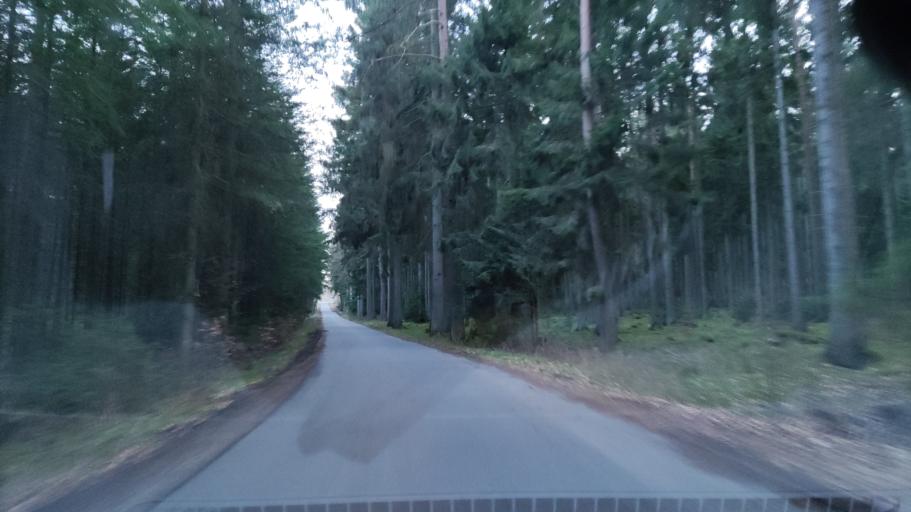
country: DE
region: Lower Saxony
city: Thomasburg
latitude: 53.1938
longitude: 10.6734
